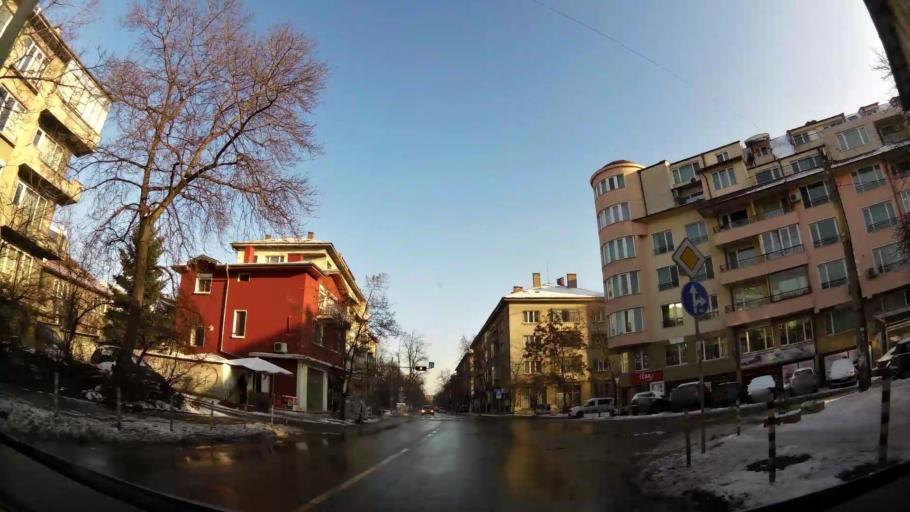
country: BG
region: Sofia-Capital
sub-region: Stolichna Obshtina
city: Sofia
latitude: 42.6851
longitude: 23.3565
